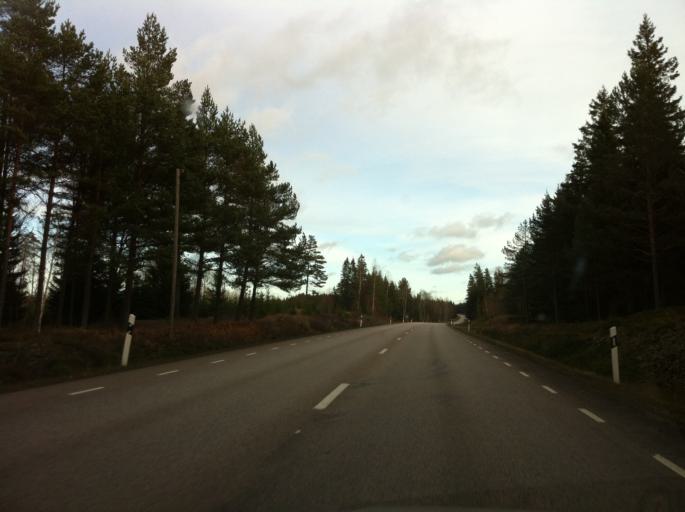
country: SE
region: Kronoberg
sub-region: Uppvidinge Kommun
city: Aseda
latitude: 57.1514
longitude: 15.3107
